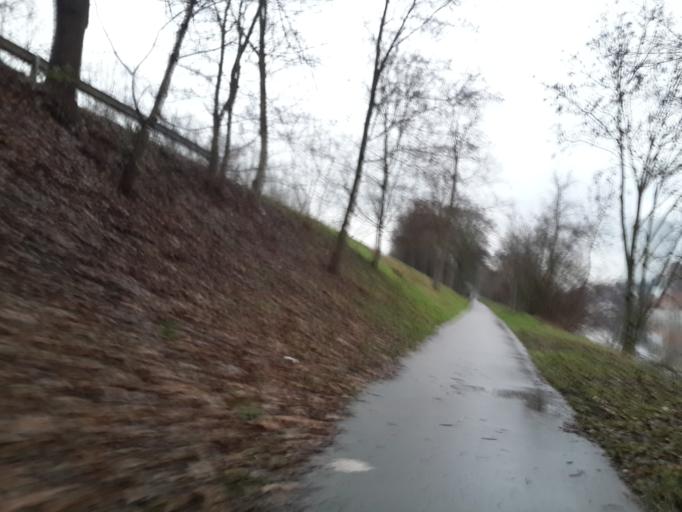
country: DE
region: Baden-Wuerttemberg
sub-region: Regierungsbezirk Stuttgart
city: Neckarsulm
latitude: 49.1697
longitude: 9.2045
